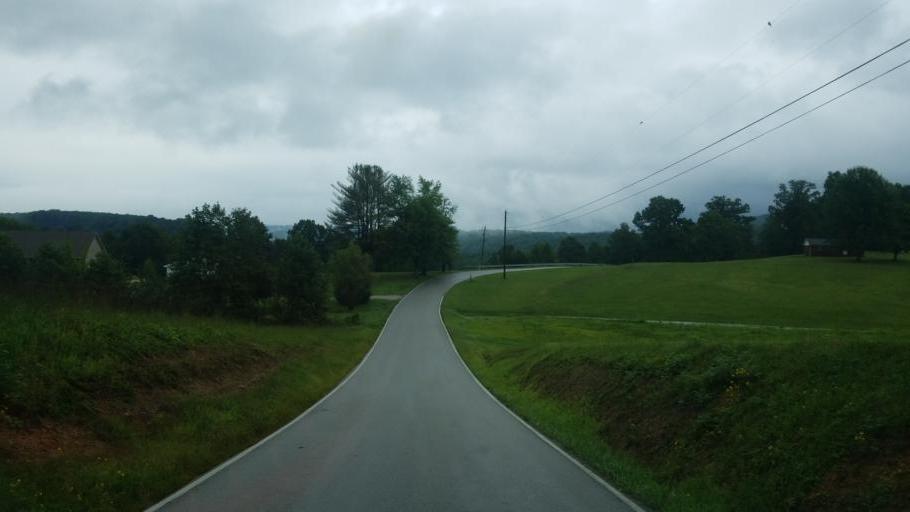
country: US
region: Kentucky
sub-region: Rowan County
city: Morehead
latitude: 38.1630
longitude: -83.5037
